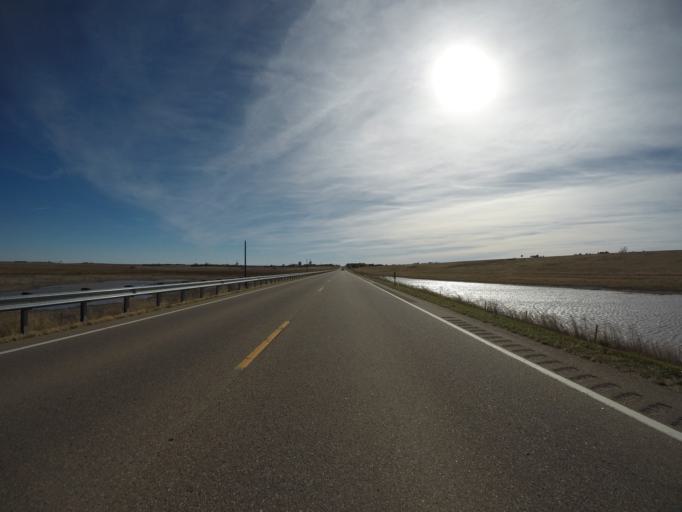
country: US
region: Colorado
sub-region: Kit Carson County
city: Burlington
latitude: 39.3418
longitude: -102.2599
